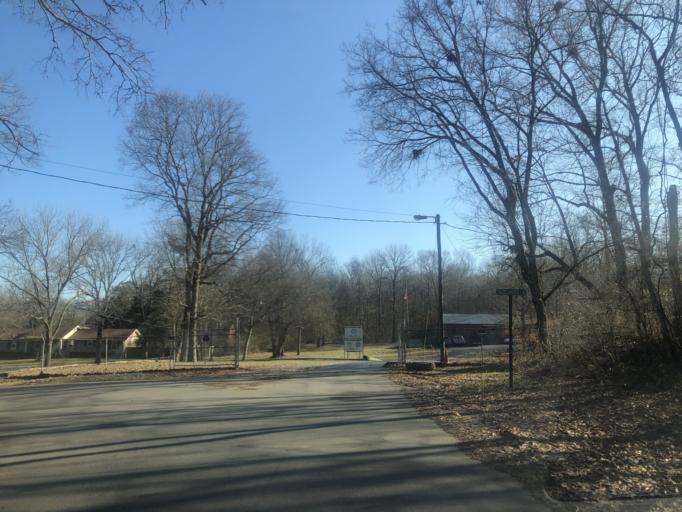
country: US
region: Tennessee
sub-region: Rutherford County
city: La Vergne
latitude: 36.0080
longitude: -86.5856
